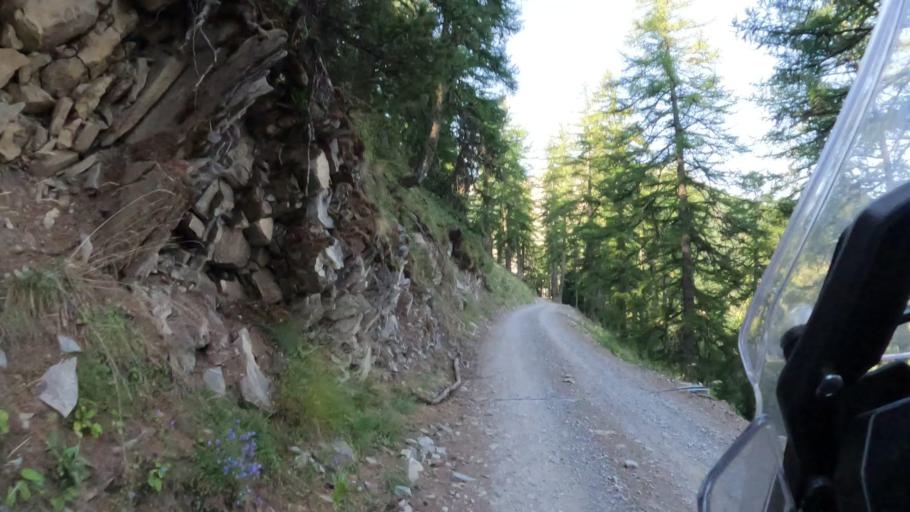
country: FR
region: Provence-Alpes-Cote d'Azur
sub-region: Departement des Hautes-Alpes
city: Guillestre
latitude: 44.5886
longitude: 6.6039
